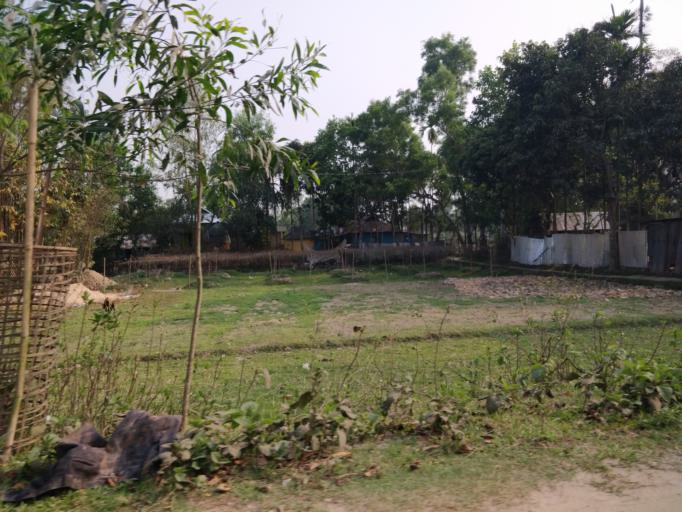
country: IN
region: Tripura
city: Khowai
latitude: 24.1293
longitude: 91.3718
